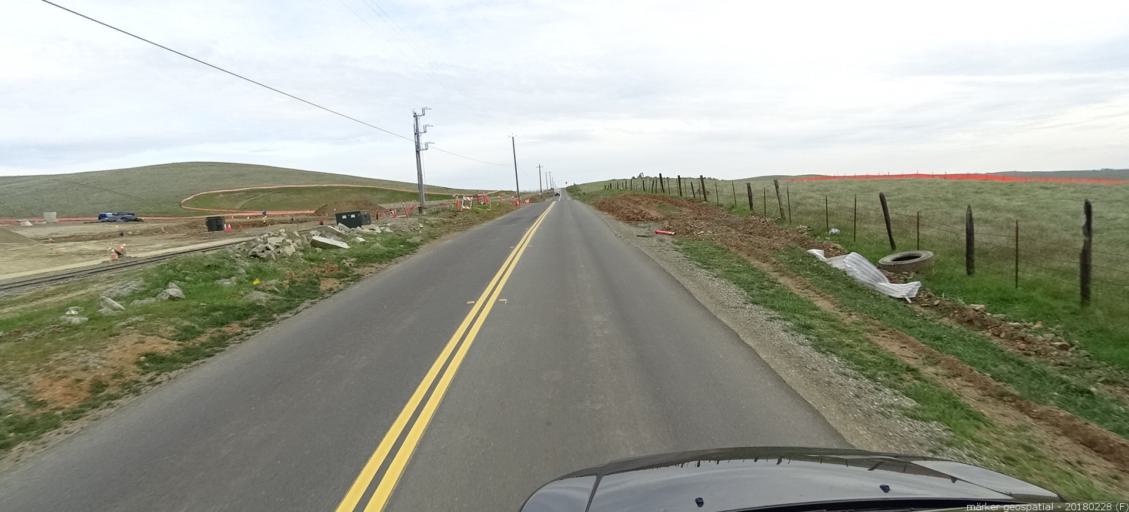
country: US
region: California
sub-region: El Dorado County
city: El Dorado Hills
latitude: 38.6340
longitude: -121.1000
